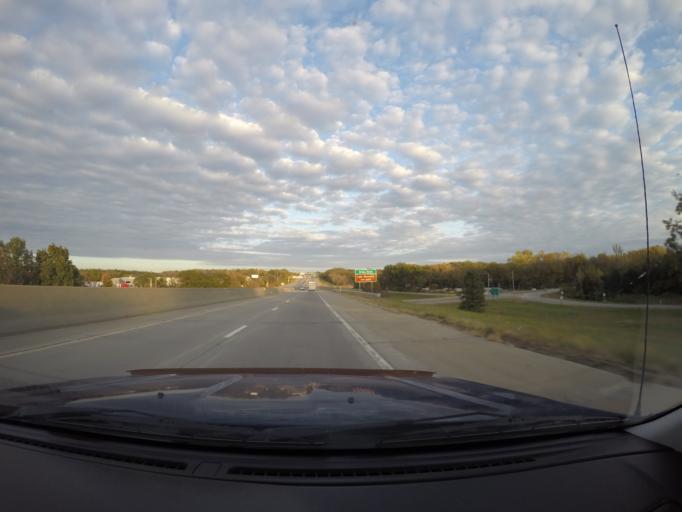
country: US
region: Kansas
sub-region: Shawnee County
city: Topeka
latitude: 39.0342
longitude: -95.6388
